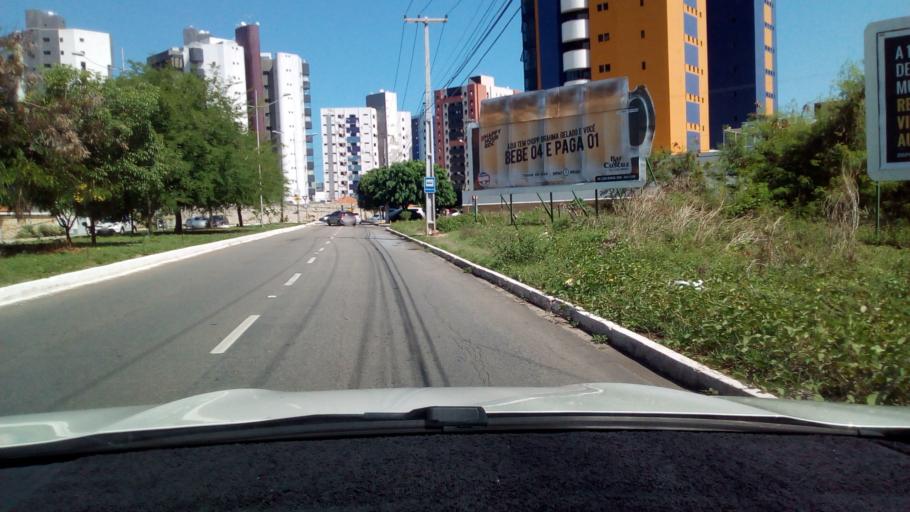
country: BR
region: Paraiba
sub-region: Joao Pessoa
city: Joao Pessoa
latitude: -7.0880
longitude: -34.8394
